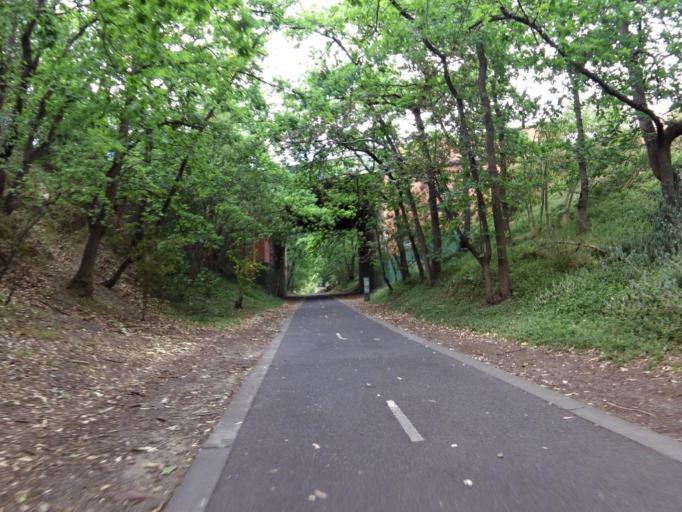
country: AU
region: Victoria
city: Balwyn
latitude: -37.8161
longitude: 145.0653
